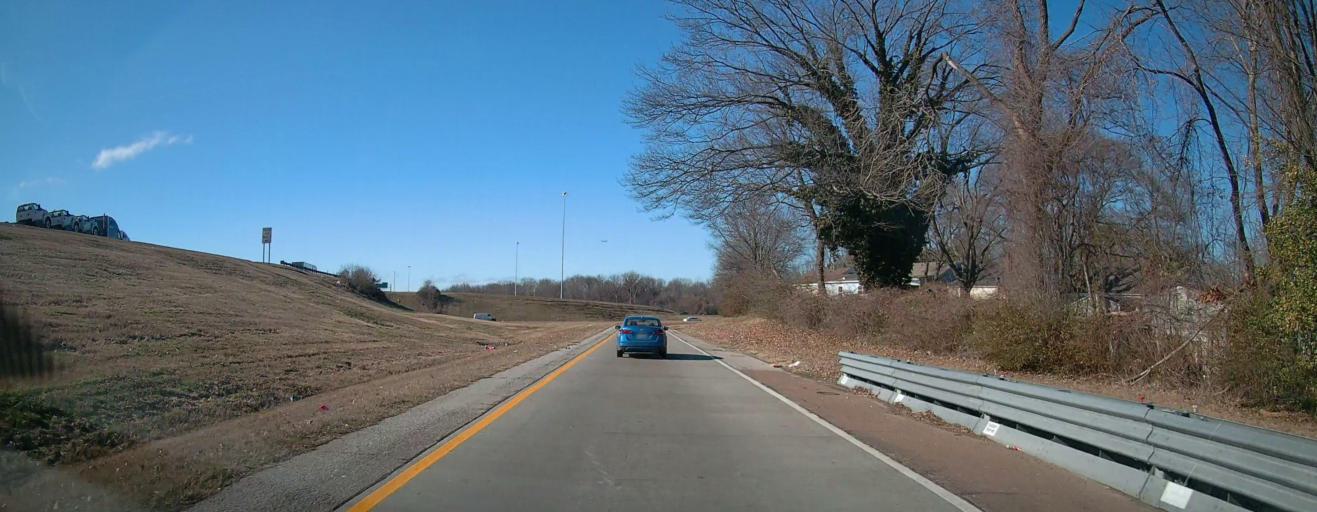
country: US
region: Tennessee
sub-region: Shelby County
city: Bartlett
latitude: 35.1927
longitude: -89.9220
